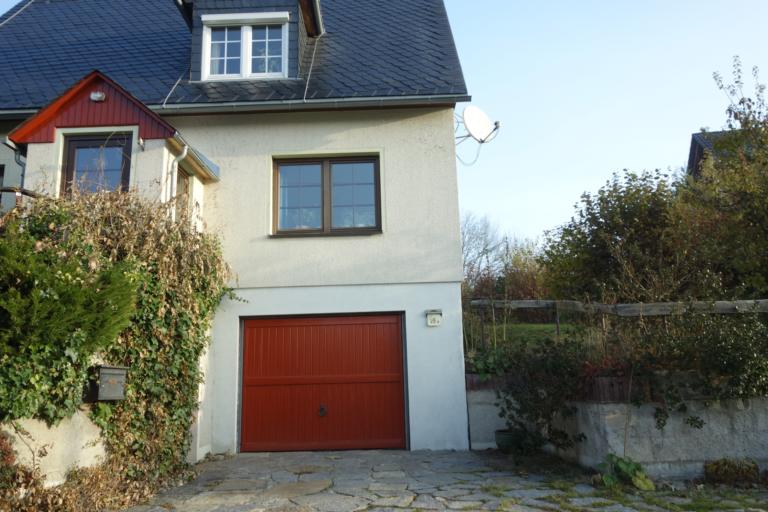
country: DE
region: Saxony
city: Lichtenberg
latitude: 50.8417
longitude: 13.4157
